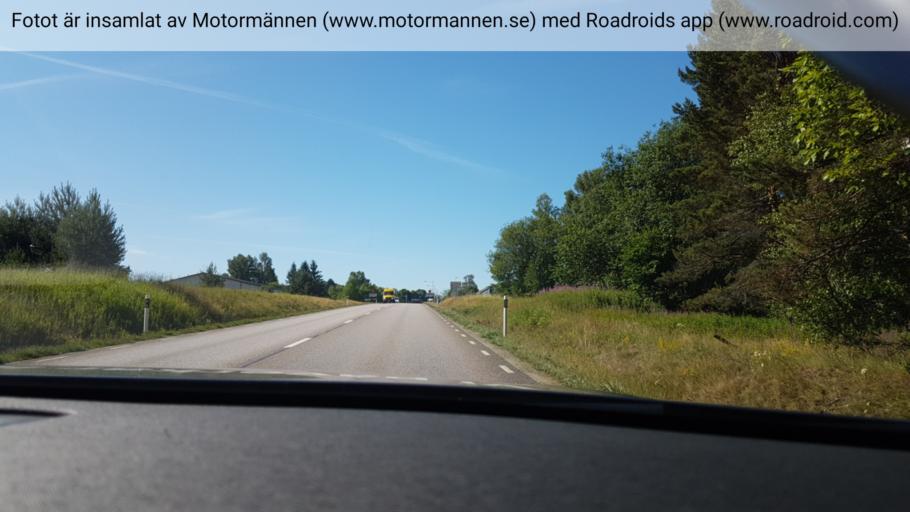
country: SE
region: Vaestra Goetaland
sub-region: Ulricehamns Kommun
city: Ulricehamn
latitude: 57.8654
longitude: 13.4309
